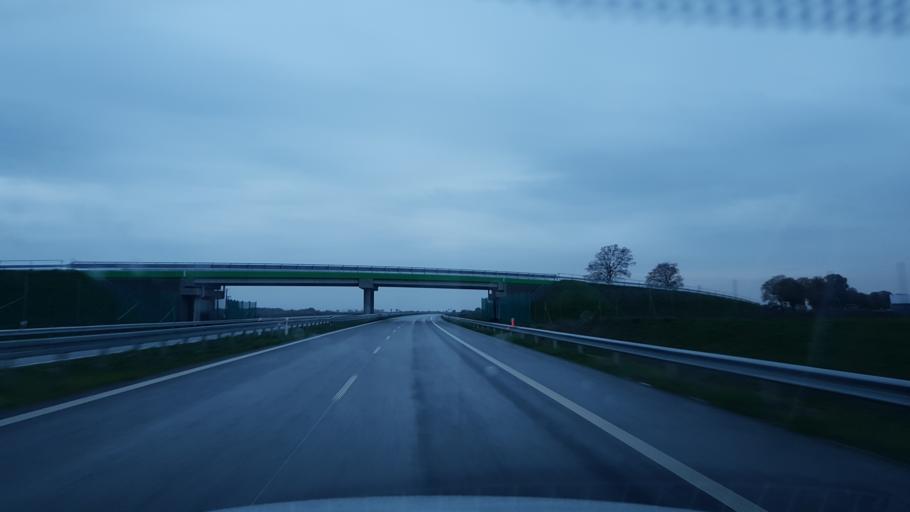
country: PL
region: West Pomeranian Voivodeship
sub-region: Powiat gryficki
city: Brojce
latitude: 53.9951
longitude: 15.4460
